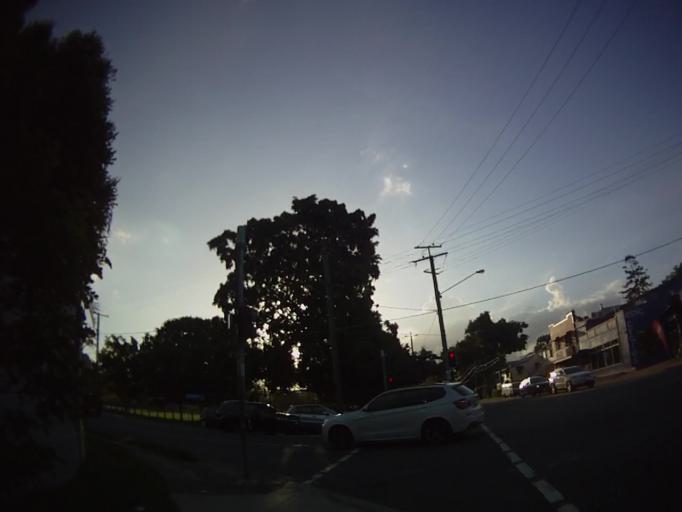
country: AU
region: Queensland
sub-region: Brisbane
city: Milton
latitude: -27.4671
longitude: 153.0016
